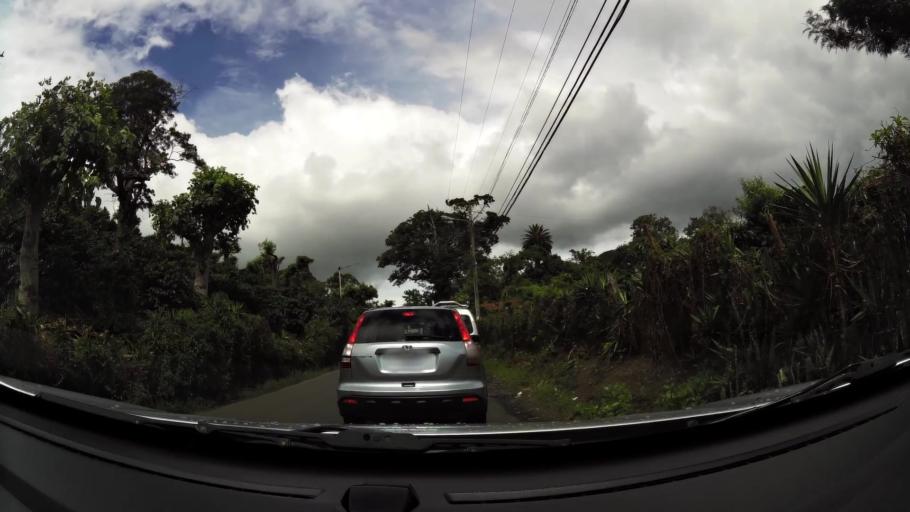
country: CR
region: Cartago
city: Tres Rios
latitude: 9.9134
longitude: -83.9893
